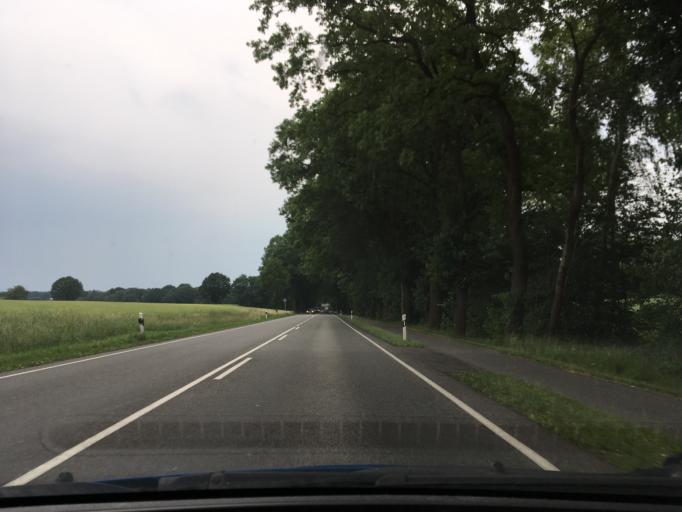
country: DE
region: Lower Saxony
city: Appel
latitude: 53.3931
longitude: 9.7931
